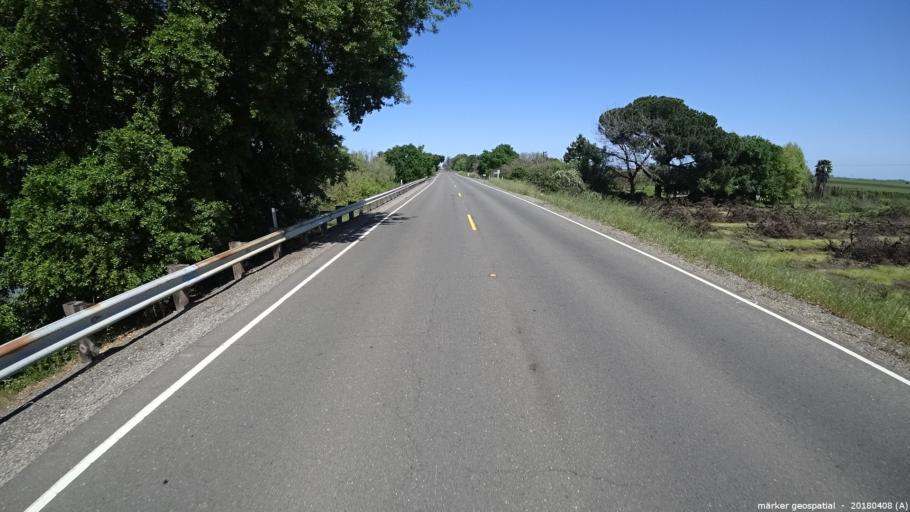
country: US
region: California
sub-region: Sacramento County
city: Walnut Grove
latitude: 38.3508
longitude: -121.5322
